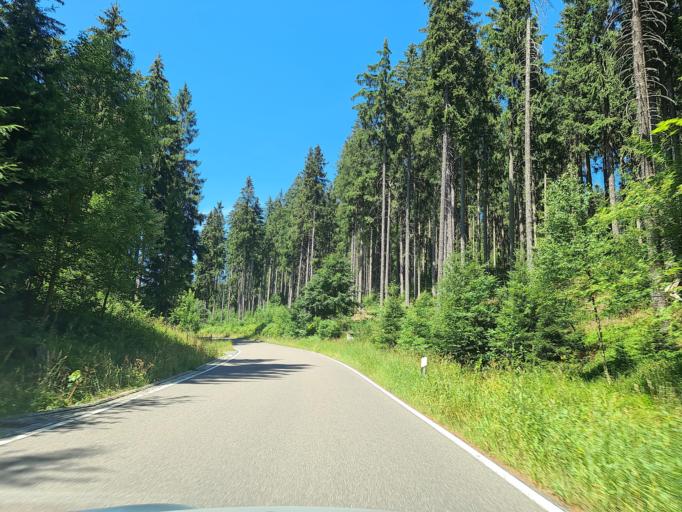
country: DE
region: Saxony
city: Rechenberg-Bienenmuhle
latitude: 50.7132
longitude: 13.5409
